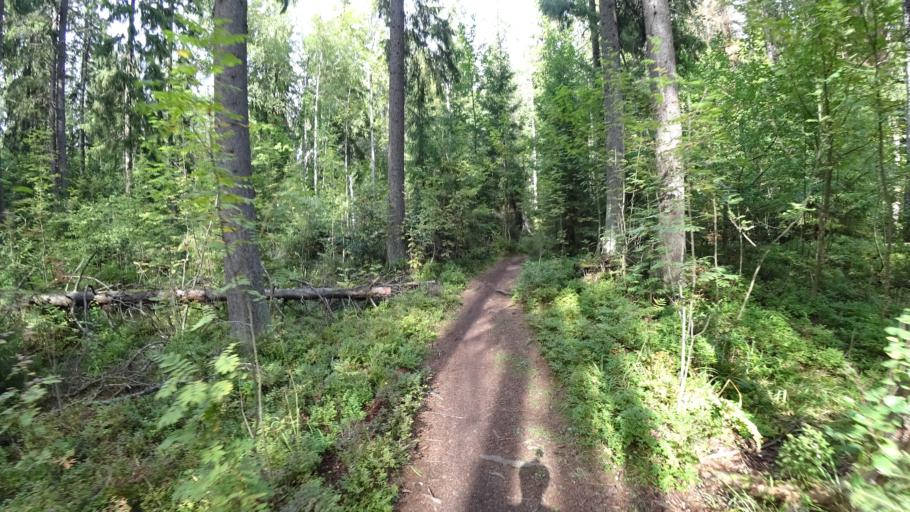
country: FI
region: Uusimaa
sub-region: Helsinki
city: Helsinki
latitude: 60.2596
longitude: 24.9199
